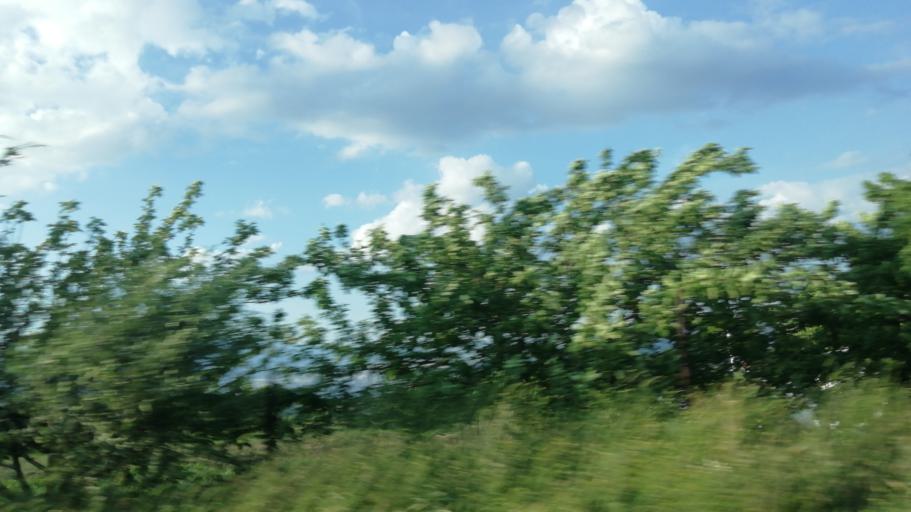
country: TR
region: Karabuk
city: Karabuk
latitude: 41.1250
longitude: 32.6163
